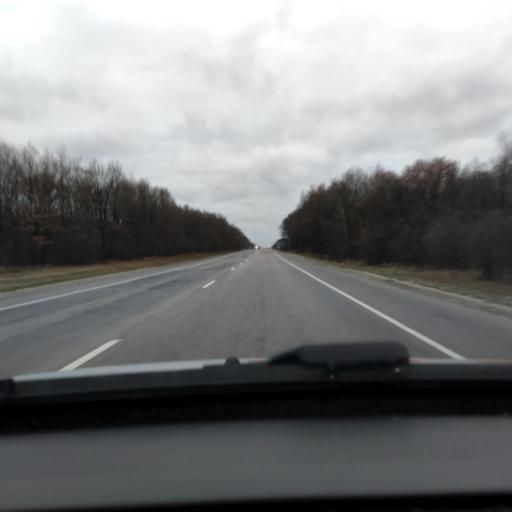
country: RU
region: Lipetsk
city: Khlevnoye
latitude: 52.3040
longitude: 39.1669
